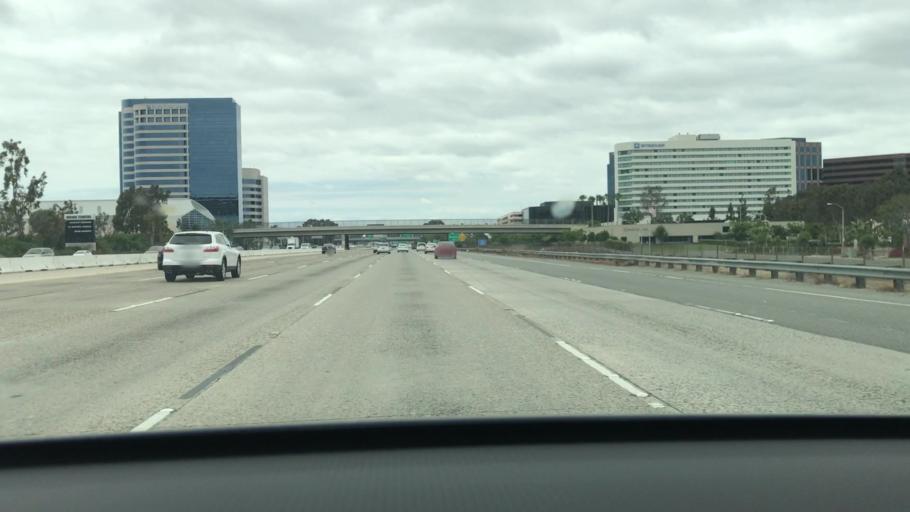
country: US
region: California
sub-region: Orange County
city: Irvine
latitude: 33.6789
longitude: -117.8480
